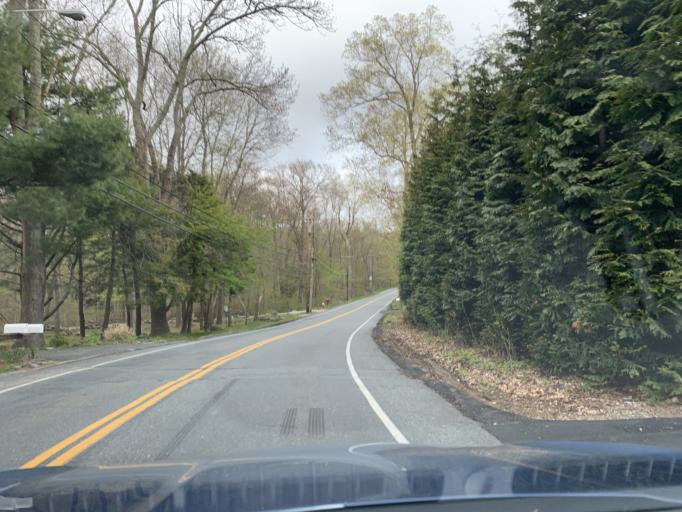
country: US
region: Rhode Island
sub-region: Washington County
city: North Kingstown
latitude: 41.5895
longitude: -71.4653
